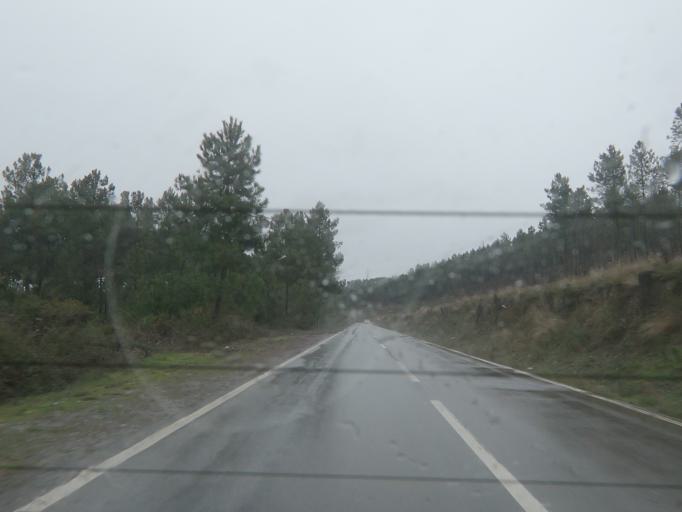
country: PT
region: Vila Real
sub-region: Sabrosa
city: Vilela
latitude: 41.2132
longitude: -7.6761
